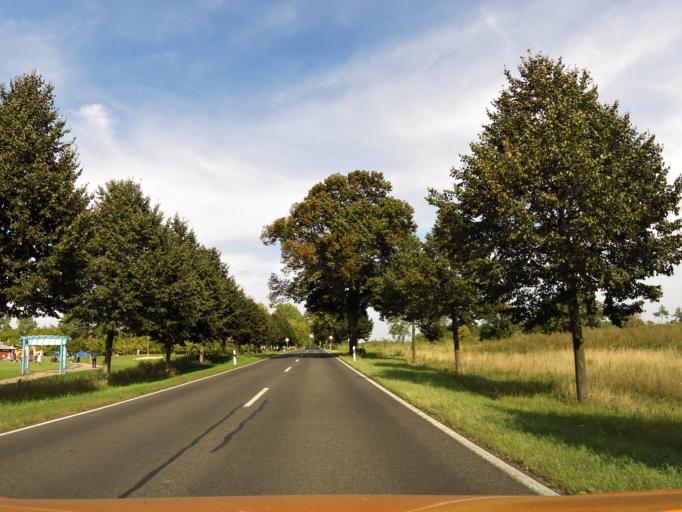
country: DE
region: Brandenburg
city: Grossbeeren
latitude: 52.3462
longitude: 13.2688
